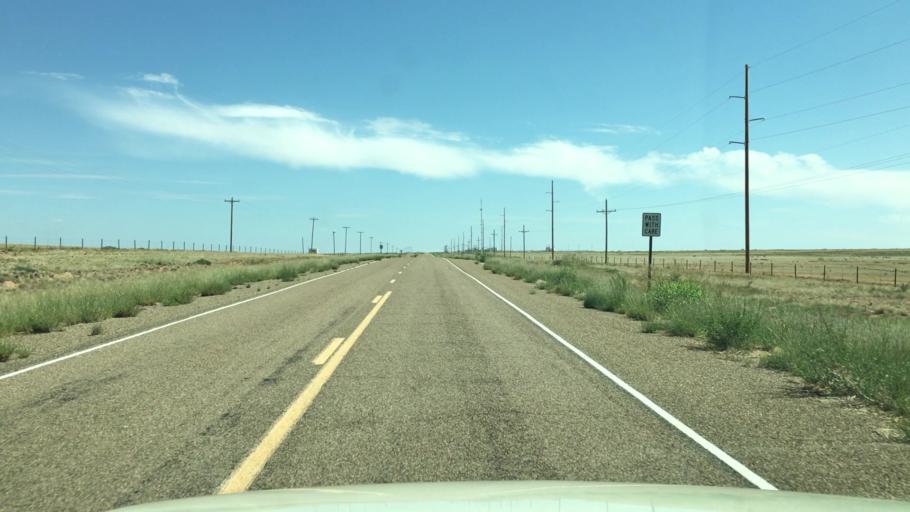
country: US
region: New Mexico
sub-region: Chaves County
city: Roswell
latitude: 33.9520
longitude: -104.5876
